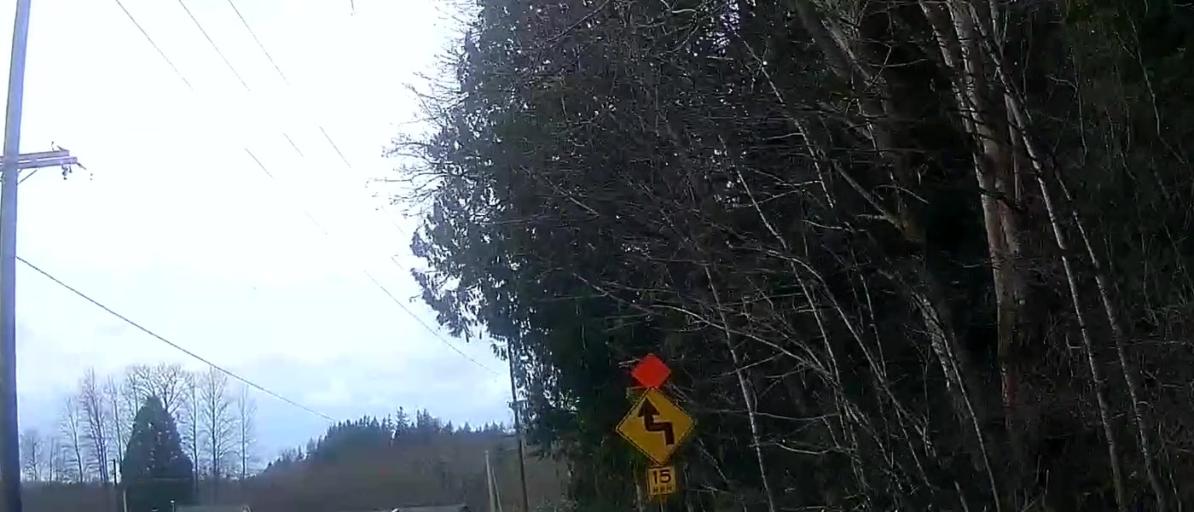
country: US
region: Washington
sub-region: Skagit County
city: Burlington
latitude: 48.5606
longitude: -122.3256
